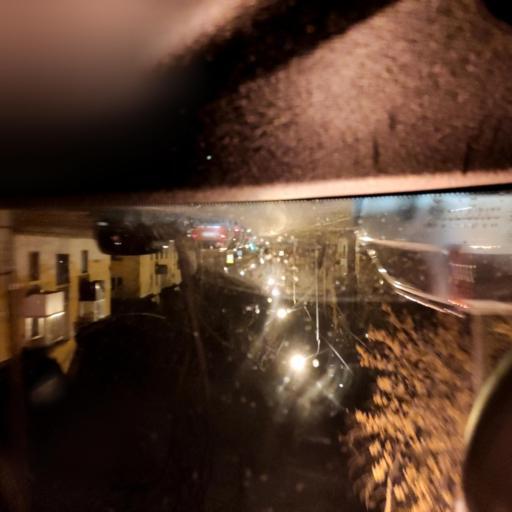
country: RU
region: Samara
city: Samara
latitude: 53.2301
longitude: 50.2594
